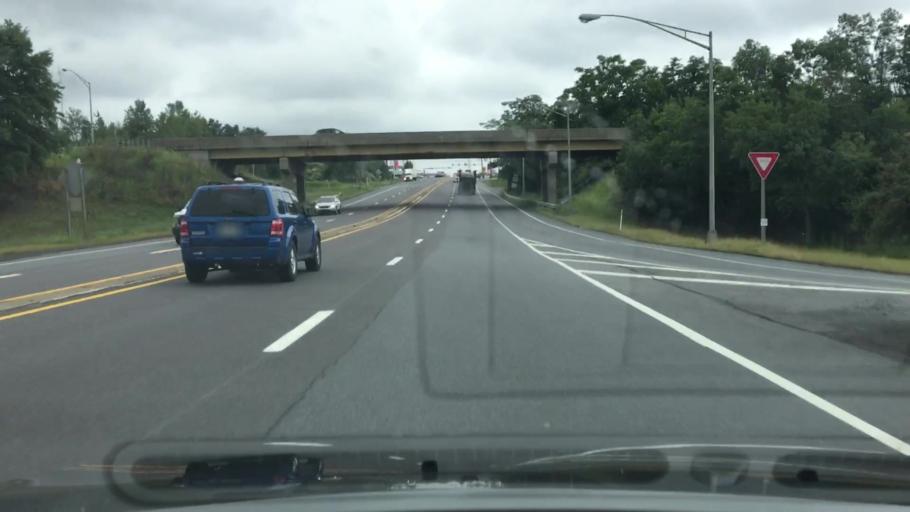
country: US
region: Pennsylvania
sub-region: Luzerne County
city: Hughestown
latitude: 41.3093
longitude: -75.7612
